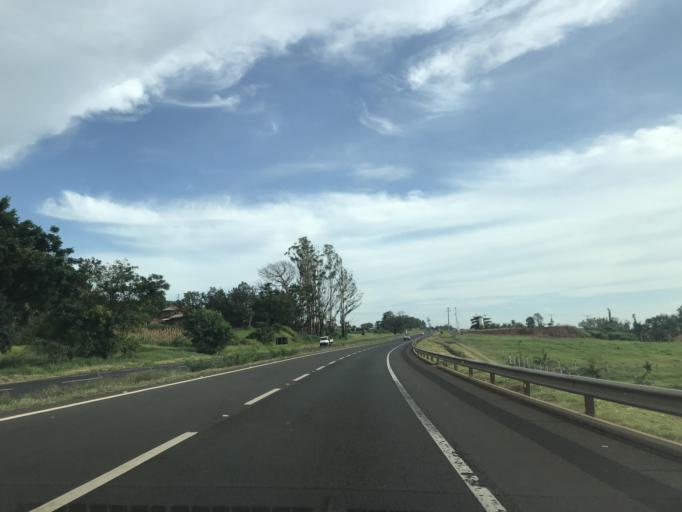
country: BR
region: Parana
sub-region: Mandaguacu
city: Mandaguacu
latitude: -23.3313
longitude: -52.1115
